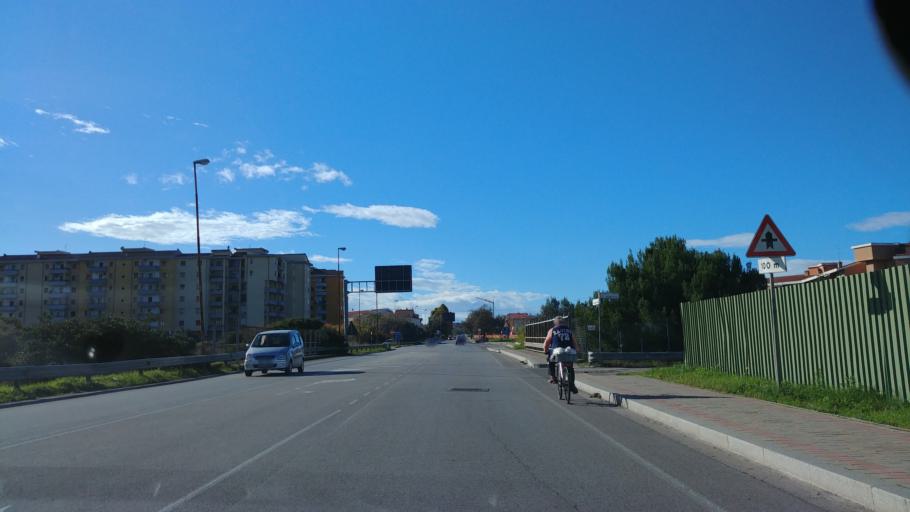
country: IT
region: Molise
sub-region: Provincia di Campobasso
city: Termoli
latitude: 41.9945
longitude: 14.9805
